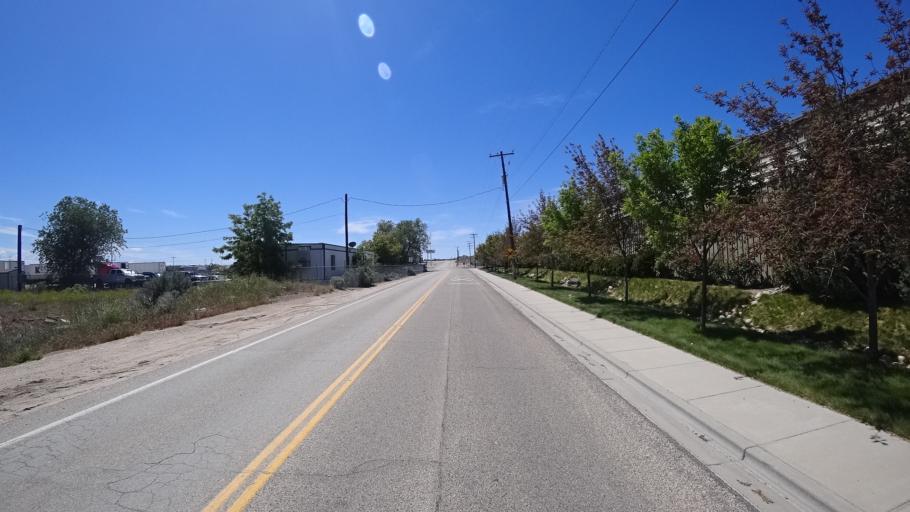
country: US
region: Idaho
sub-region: Ada County
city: Boise
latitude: 43.5646
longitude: -116.1835
